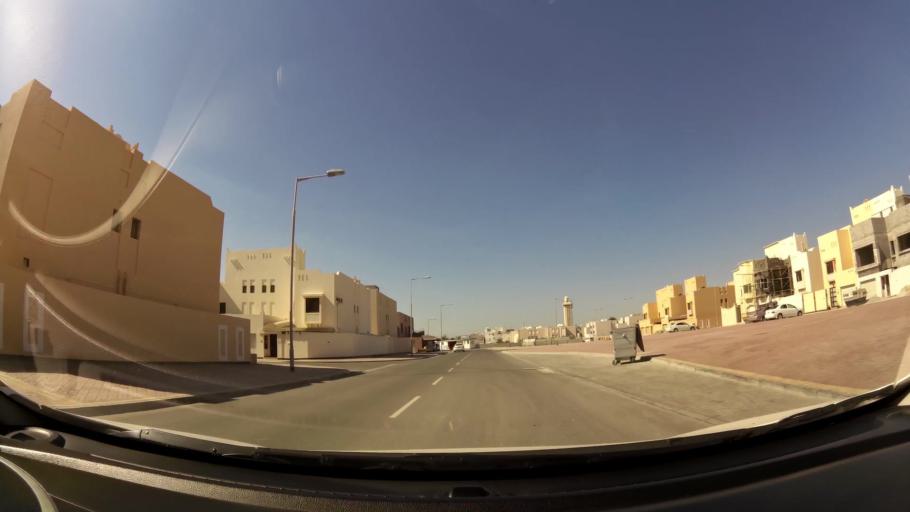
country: BH
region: Muharraq
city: Al Muharraq
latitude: 26.2477
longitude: 50.6318
